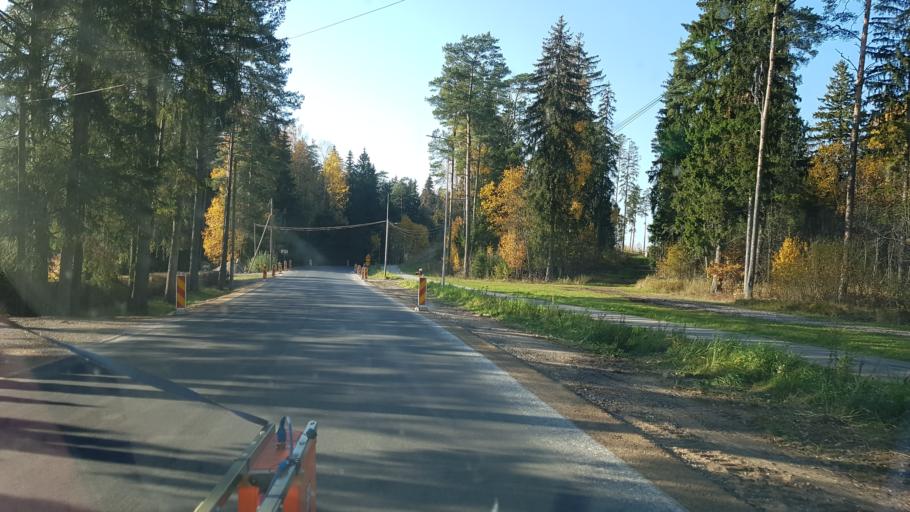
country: EE
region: Vorumaa
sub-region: Antsla vald
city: Vana-Antsla
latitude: 57.8311
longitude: 26.5154
